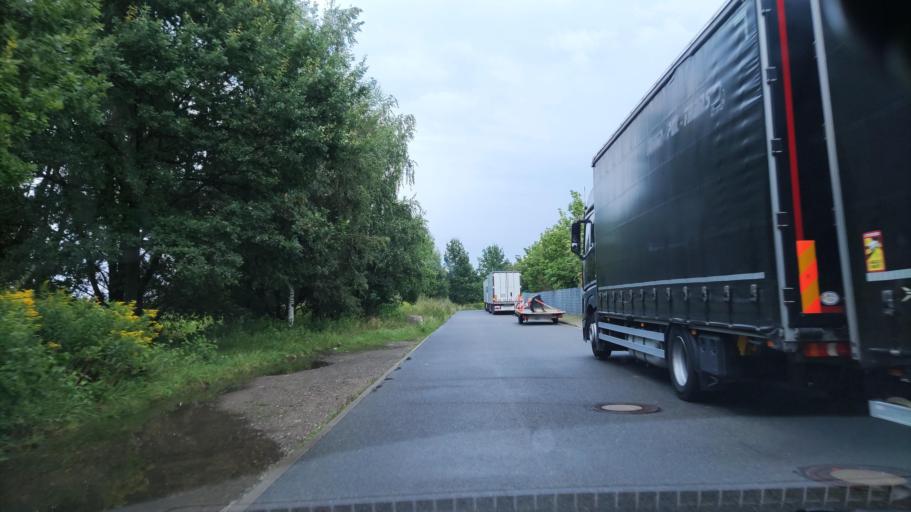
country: DE
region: Lower Saxony
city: Sarstedt
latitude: 52.2765
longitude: 9.8518
